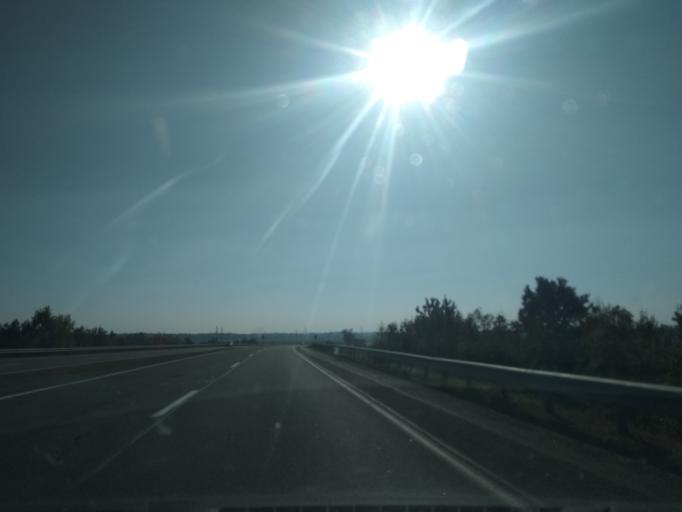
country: BY
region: Brest
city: Horad Kobryn
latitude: 52.2071
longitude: 24.4211
